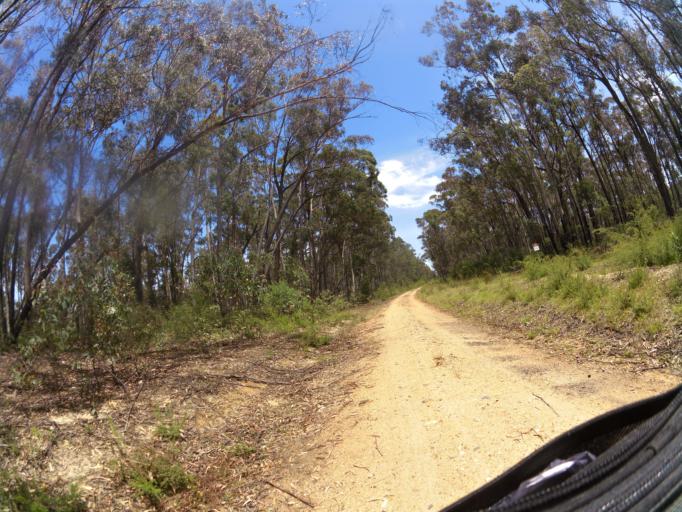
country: AU
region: Victoria
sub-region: East Gippsland
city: Lakes Entrance
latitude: -37.7557
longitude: 147.9684
